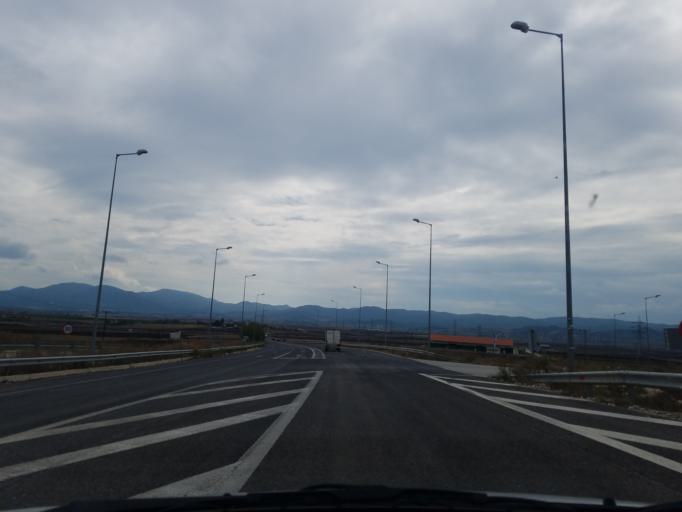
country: GR
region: Central Greece
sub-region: Nomos Fthiotidos
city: Omvriaki
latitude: 39.0848
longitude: 22.3084
